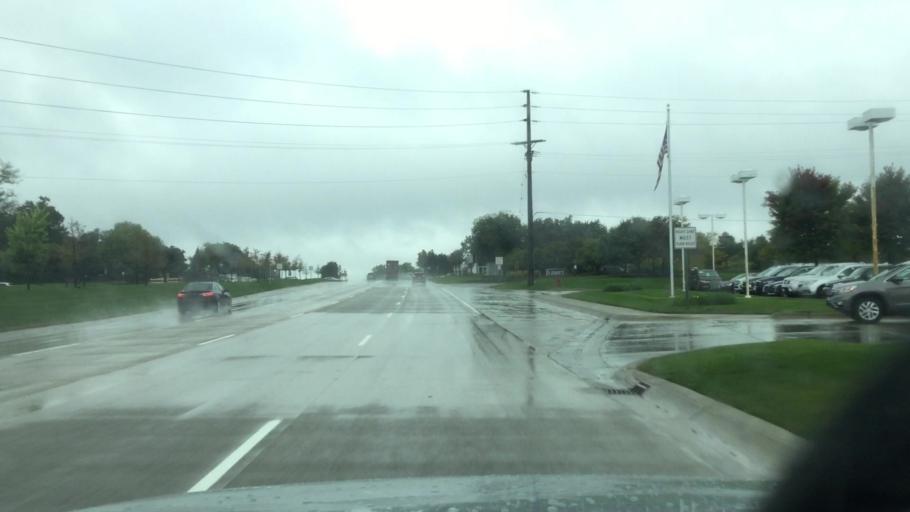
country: US
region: Michigan
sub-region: Oakland County
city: Sylvan Lake
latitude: 42.6133
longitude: -83.3079
